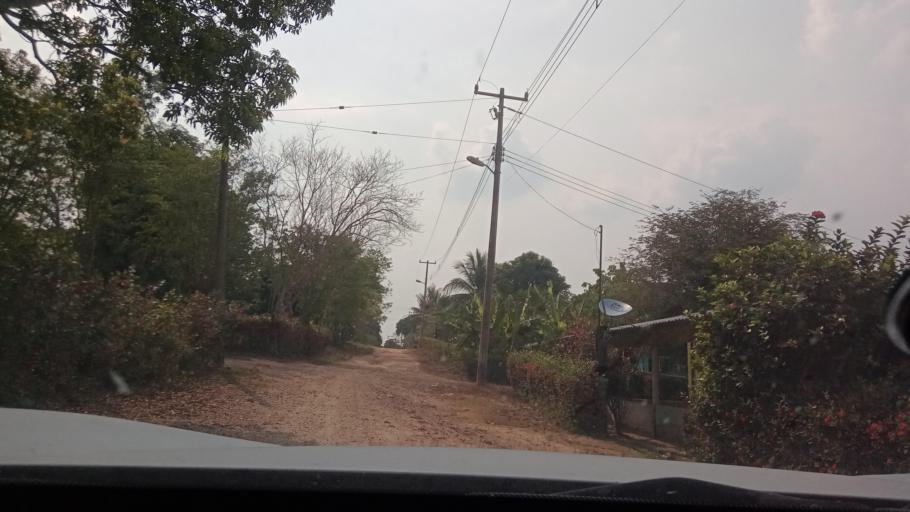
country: MX
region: Tabasco
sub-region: Huimanguillo
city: Francisco Rueda
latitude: 17.6910
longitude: -93.8324
